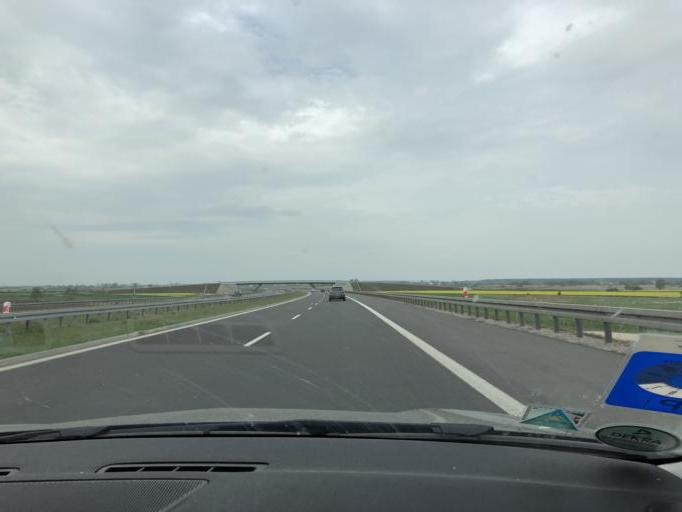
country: PL
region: Subcarpathian Voivodeship
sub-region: Powiat przeworski
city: Rozborz
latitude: 50.0696
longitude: 22.5565
